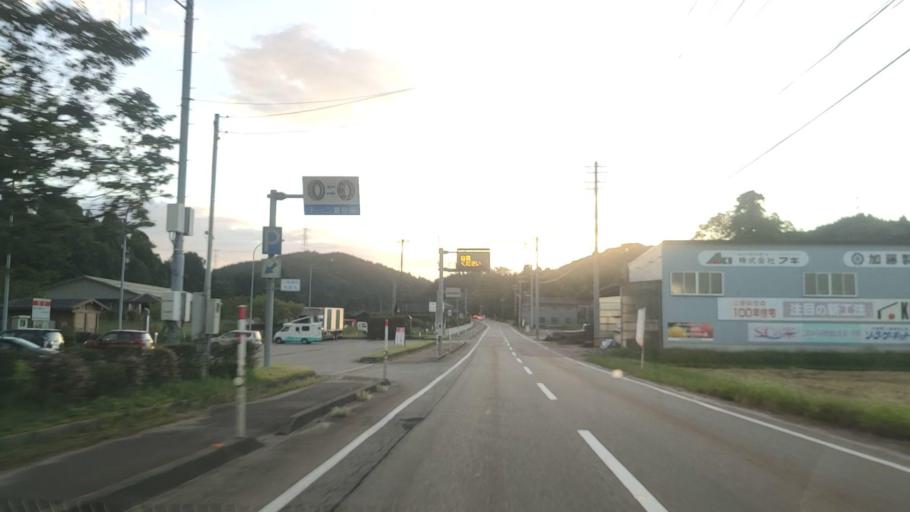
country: JP
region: Toyama
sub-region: Oyabe Shi
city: Oyabe
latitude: 36.6318
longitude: 136.8244
